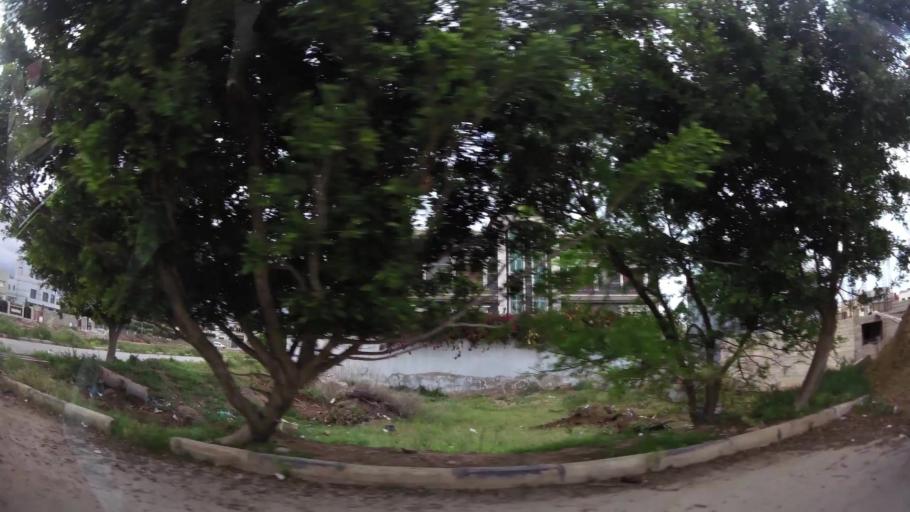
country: MA
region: Oriental
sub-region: Nador
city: Nador
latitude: 35.1615
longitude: -2.9148
